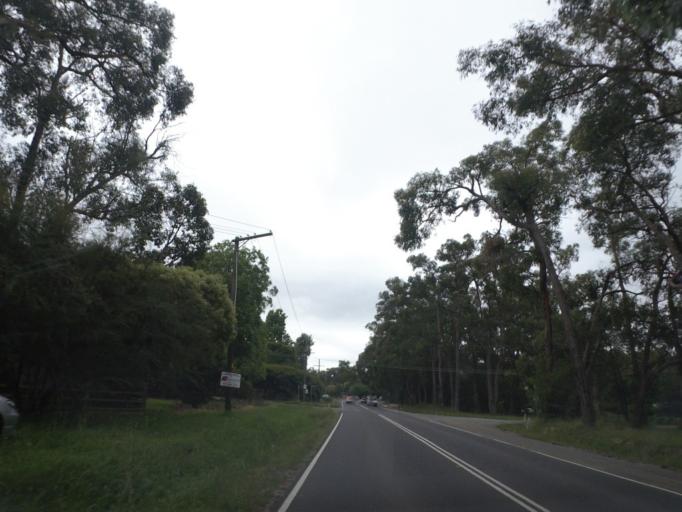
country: AU
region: Victoria
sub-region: Yarra Ranges
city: Mount Evelyn
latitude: -37.7942
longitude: 145.3758
